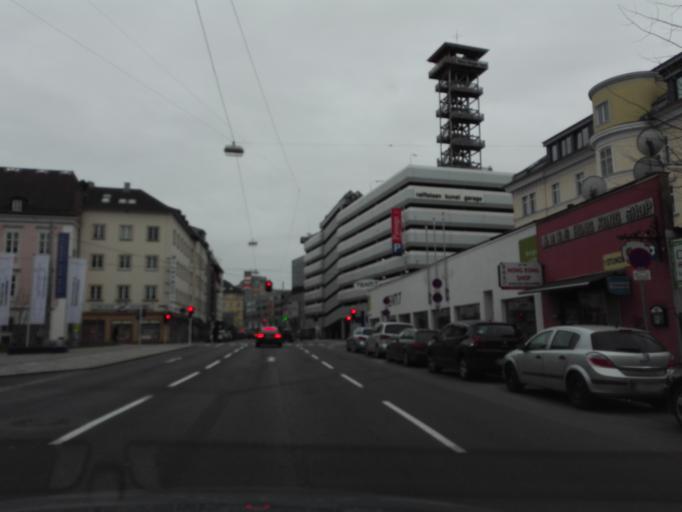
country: AT
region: Upper Austria
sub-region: Linz Stadt
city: Linz
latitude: 48.3044
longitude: 14.2908
